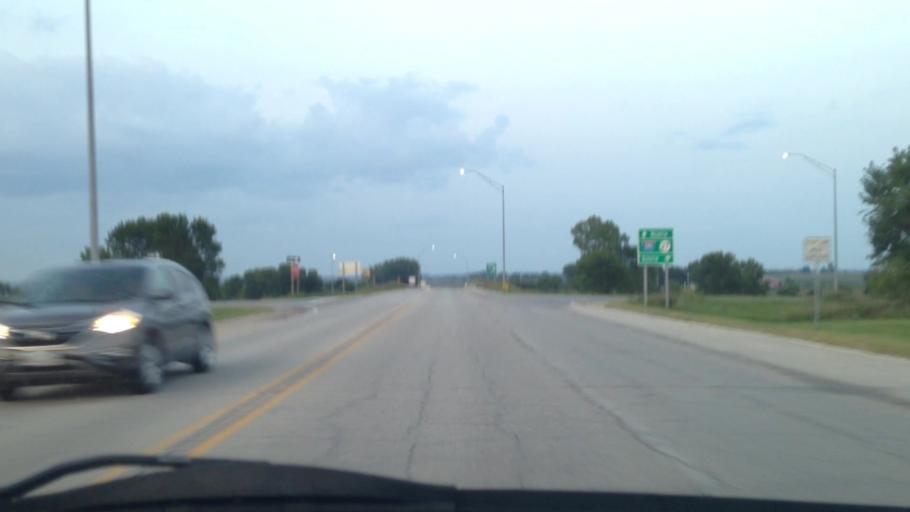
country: US
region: Iowa
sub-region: Benton County
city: Urbana
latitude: 42.2278
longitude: -91.8696
